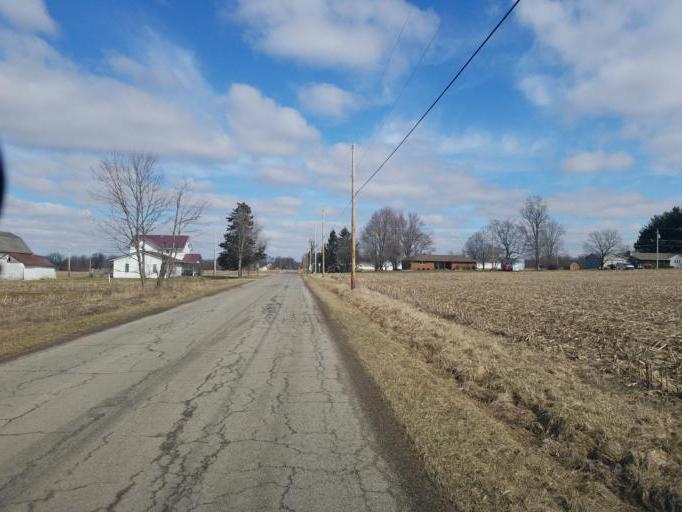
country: US
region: Ohio
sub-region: Crawford County
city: Galion
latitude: 40.6963
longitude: -82.7839
